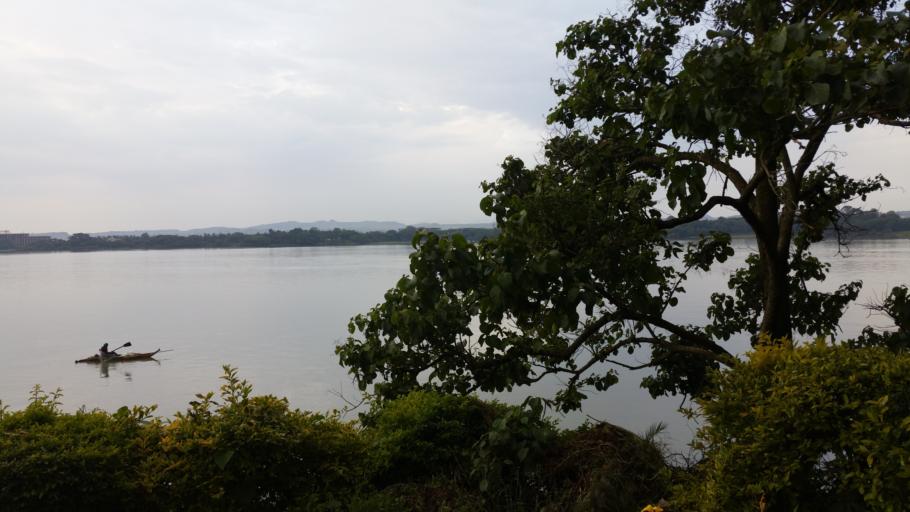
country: ET
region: Amhara
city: Bahir Dar
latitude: 11.6001
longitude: 37.3833
